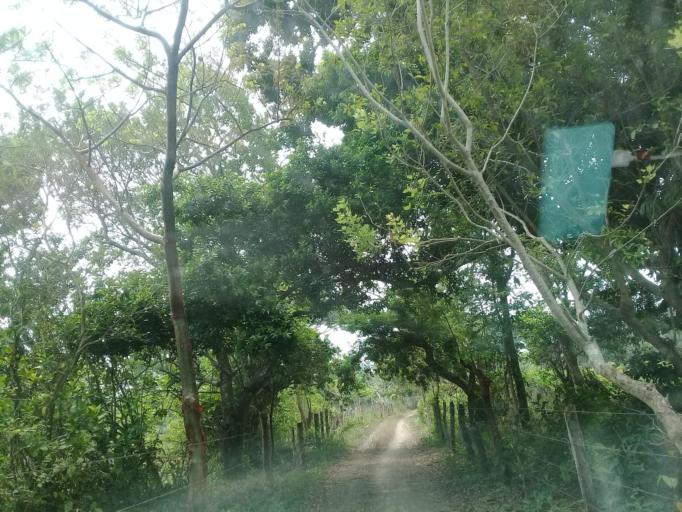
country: MX
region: Veracruz
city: El Tejar
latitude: 19.0573
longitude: -96.1978
